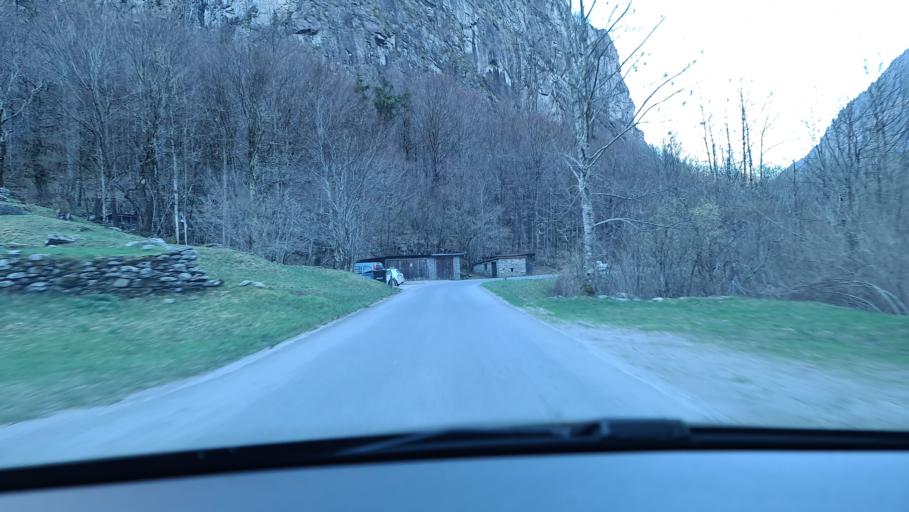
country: CH
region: Ticino
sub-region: Vallemaggia District
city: Cevio
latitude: 46.3797
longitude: 8.5434
